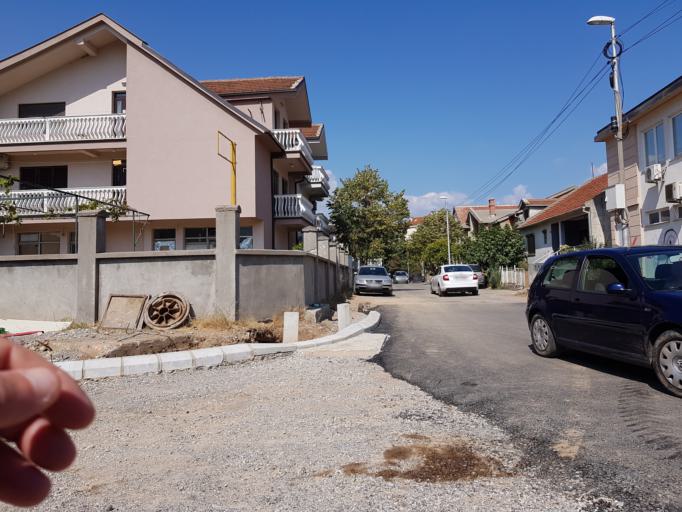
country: ME
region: Podgorica
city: Podgorica
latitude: 42.4304
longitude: 19.2774
